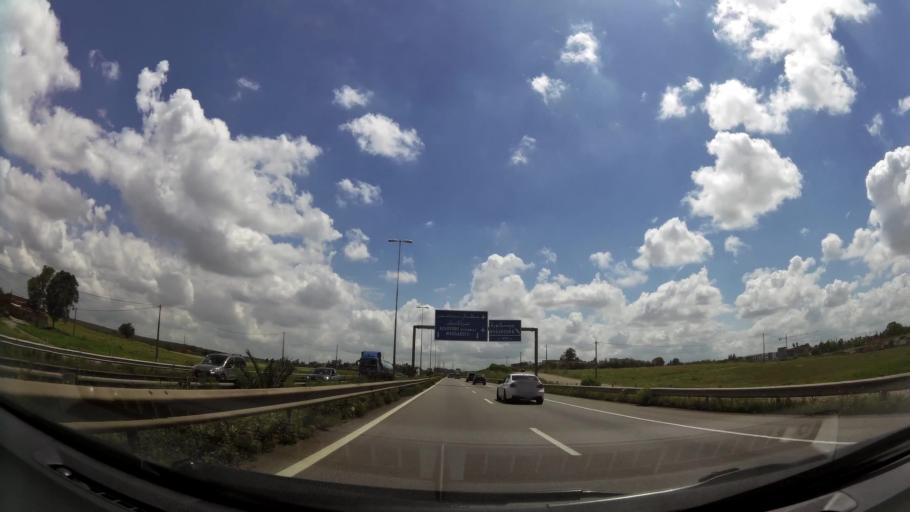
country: MA
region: Grand Casablanca
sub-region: Nouaceur
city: Bouskoura
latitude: 33.4451
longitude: -7.6321
